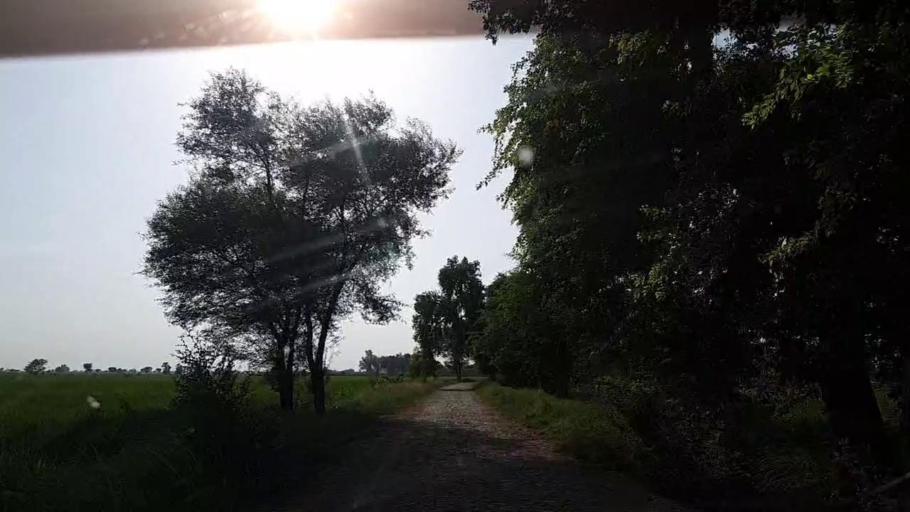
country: PK
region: Sindh
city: Khanpur
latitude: 27.8422
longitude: 69.3736
